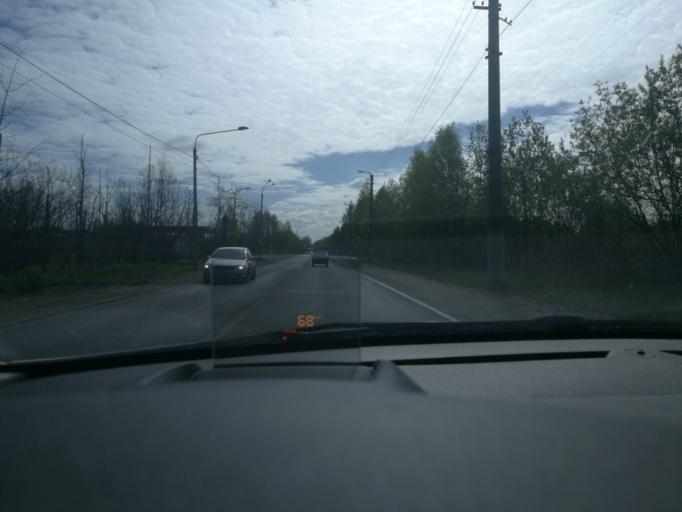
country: RU
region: Arkhangelskaya
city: Arkhangel'sk
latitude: 64.5980
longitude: 40.5583
